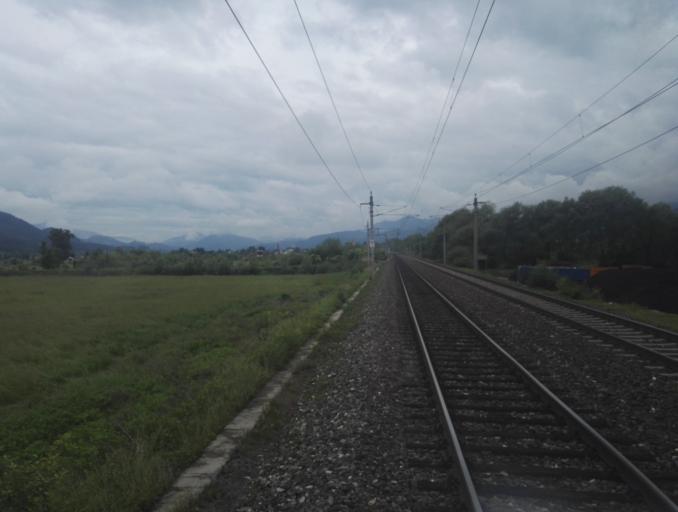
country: AT
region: Styria
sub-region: Politischer Bezirk Bruck-Muerzzuschlag
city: Muerzhofen
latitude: 47.4776
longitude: 15.3910
